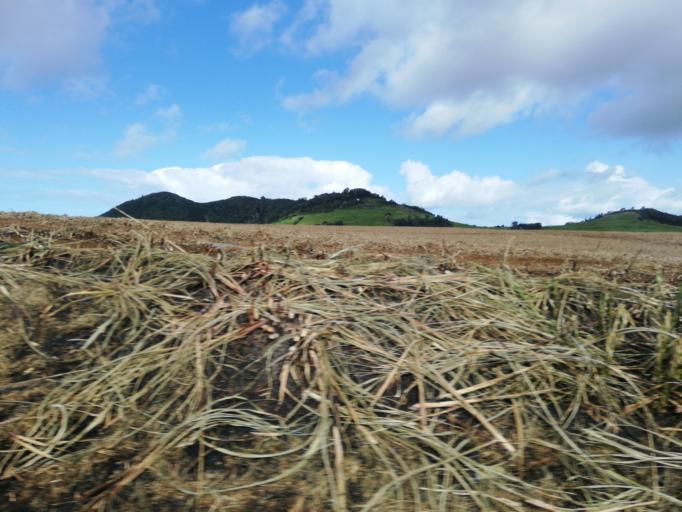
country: MU
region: Flacq
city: Grande Riviere Sud Est
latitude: -20.2841
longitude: 57.7550
